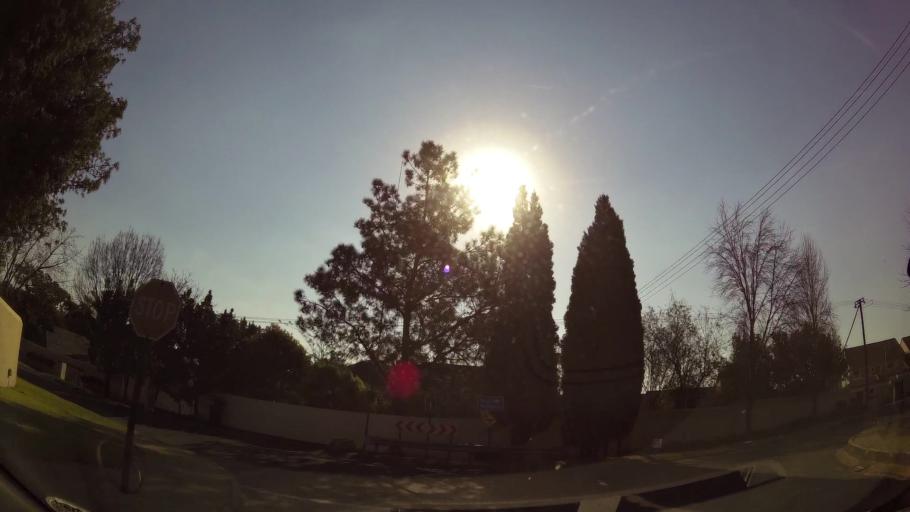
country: ZA
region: Gauteng
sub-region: City of Johannesburg Metropolitan Municipality
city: Diepsloot
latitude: -26.0687
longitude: 28.0115
